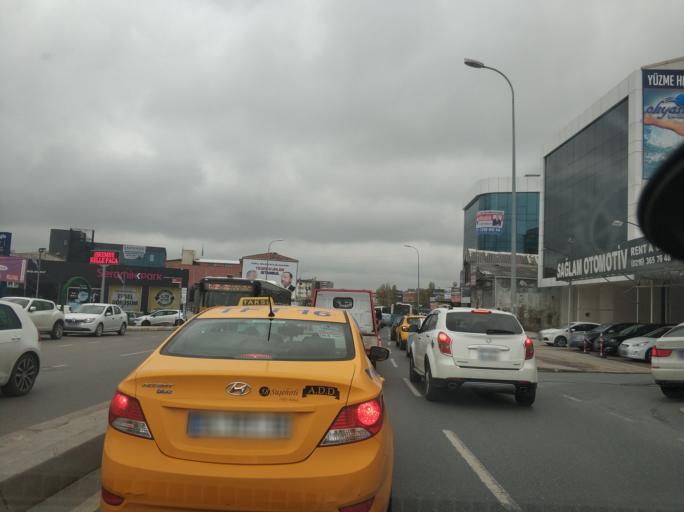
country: TR
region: Istanbul
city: Umraniye
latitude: 41.0198
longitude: 29.1303
